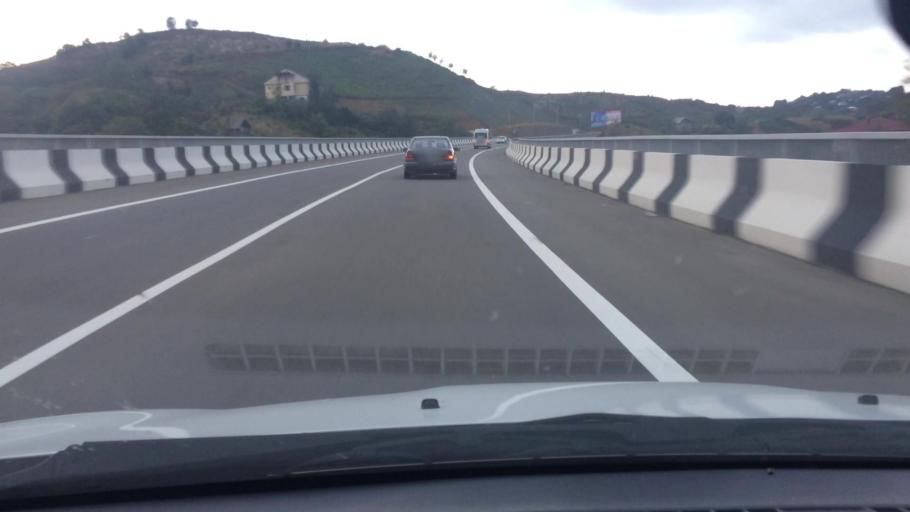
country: GE
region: Ajaria
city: Makhinjauri
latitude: 41.7218
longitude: 41.7496
